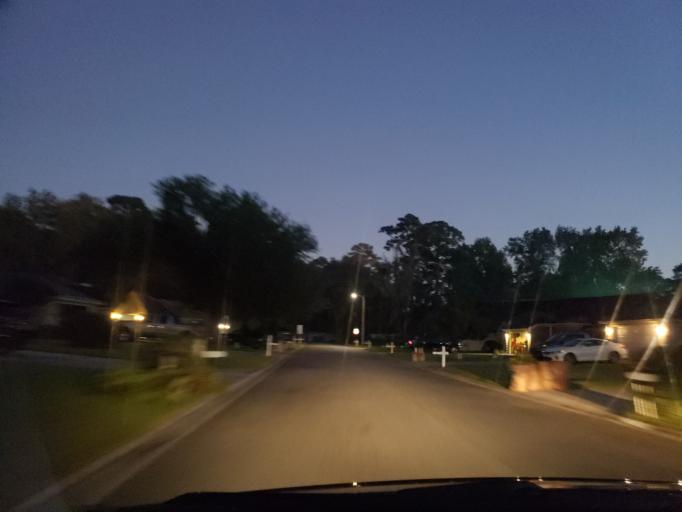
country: US
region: Georgia
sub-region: Chatham County
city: Isle of Hope
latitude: 31.9921
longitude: -81.0688
